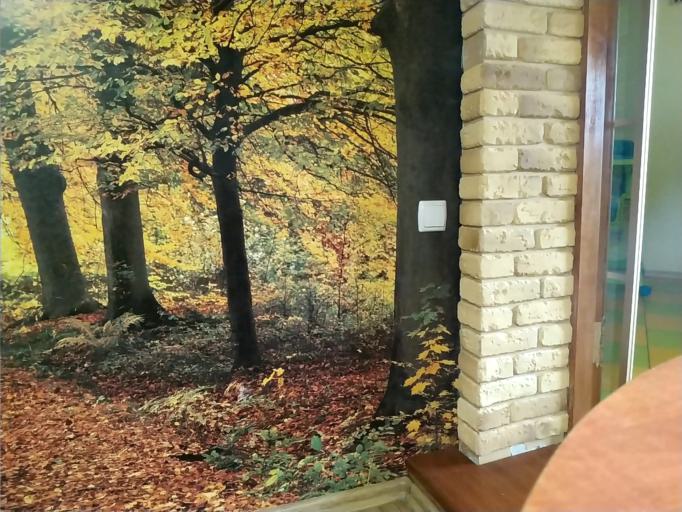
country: RU
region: Smolensk
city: Dorogobuzh
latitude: 54.8724
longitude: 33.3117
